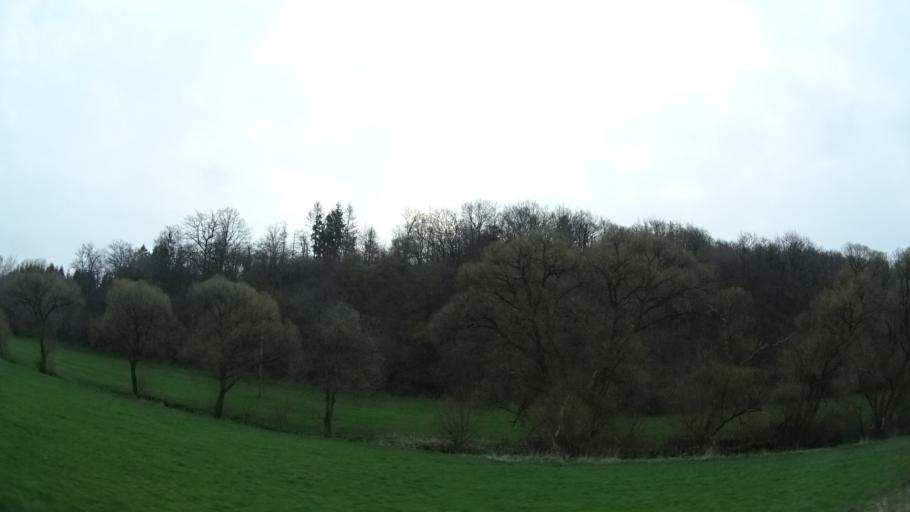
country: DE
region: Rheinland-Pfalz
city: Schmissberg
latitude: 49.6483
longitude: 7.1967
